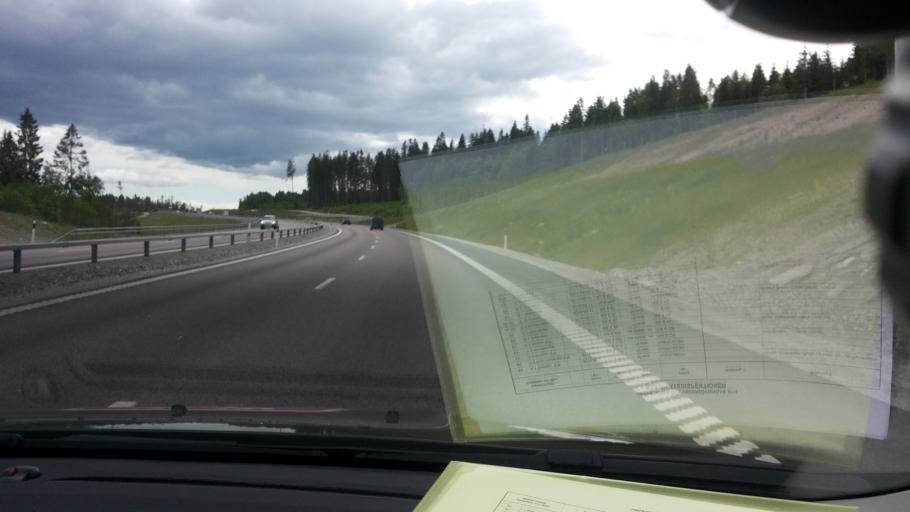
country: SE
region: Vaesternorrland
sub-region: Sundsvalls Kommun
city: Stockvik
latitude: 62.3202
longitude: 17.3394
